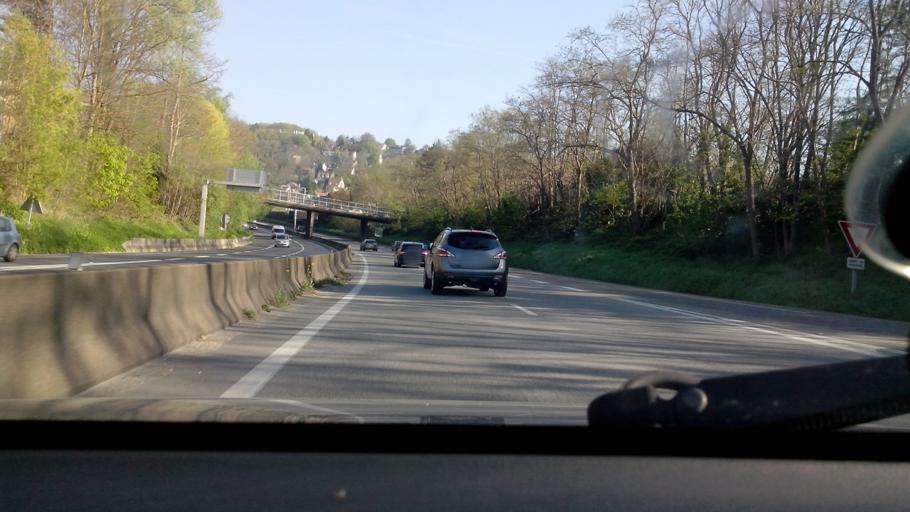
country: FR
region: Ile-de-France
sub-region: Departement de l'Essonne
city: Orsay
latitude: 48.7022
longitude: 2.1930
